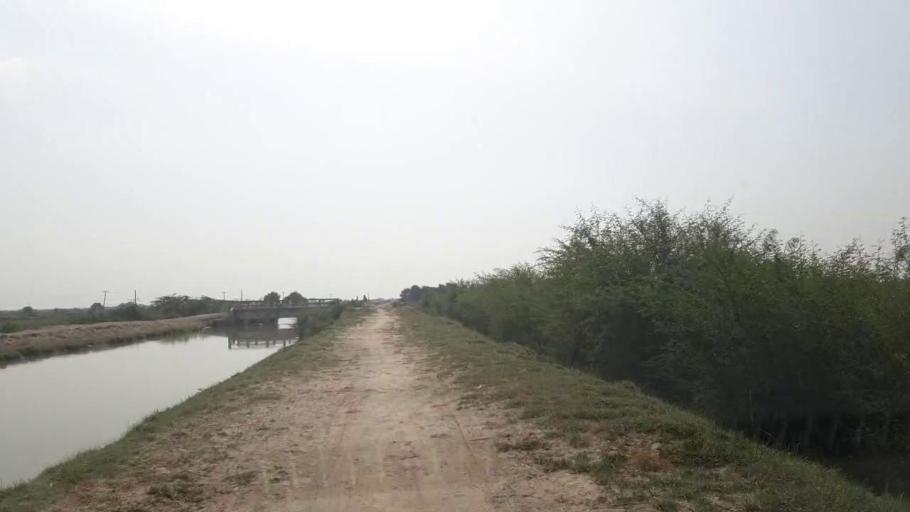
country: PK
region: Sindh
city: Badin
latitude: 24.5545
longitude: 68.8496
